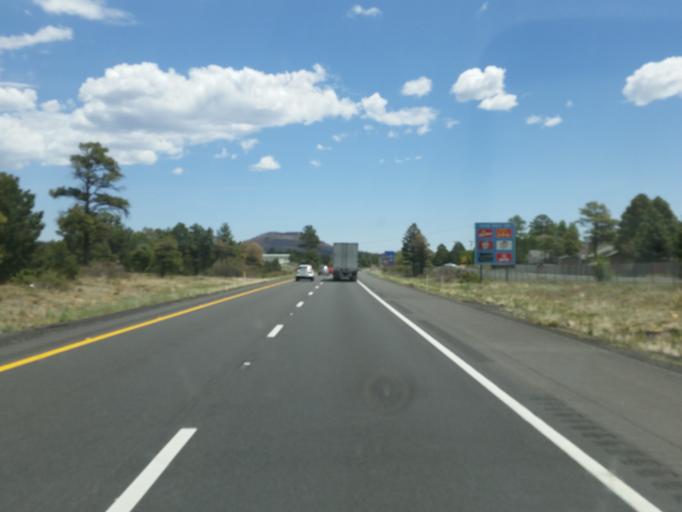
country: US
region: Arizona
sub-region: Coconino County
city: Flagstaff
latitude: 35.2090
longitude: -111.5982
